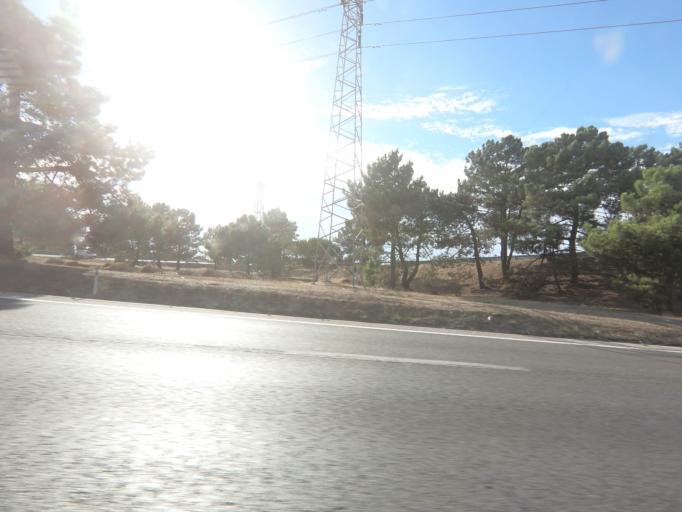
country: PT
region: Setubal
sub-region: Barreiro
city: Santo Antonio da Charneca
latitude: 38.6226
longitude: -9.0355
